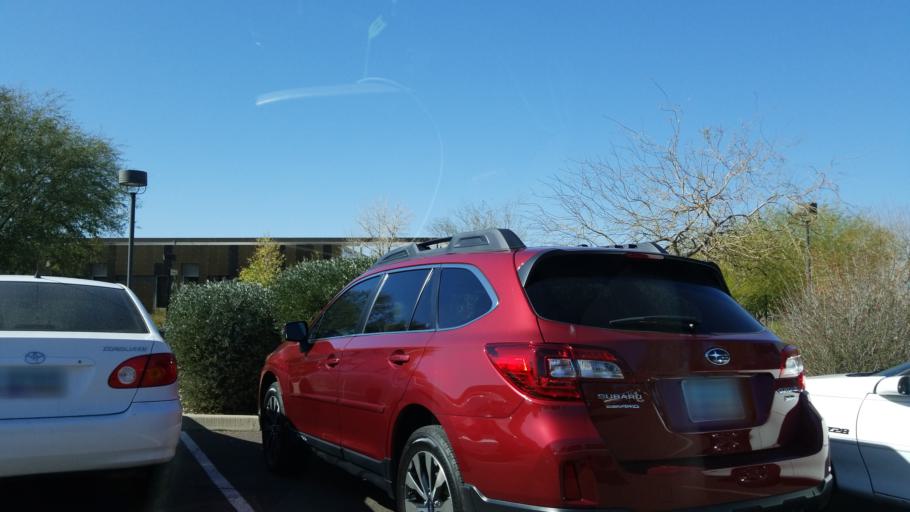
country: US
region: Arizona
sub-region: Maricopa County
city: Scottsdale
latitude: 33.5139
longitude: -111.8824
